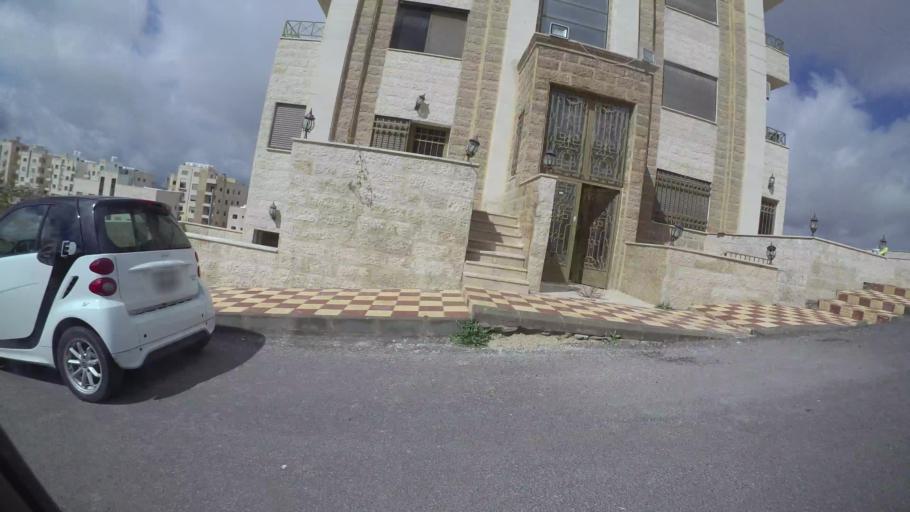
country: JO
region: Amman
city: Al Jubayhah
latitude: 32.0667
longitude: 35.8766
